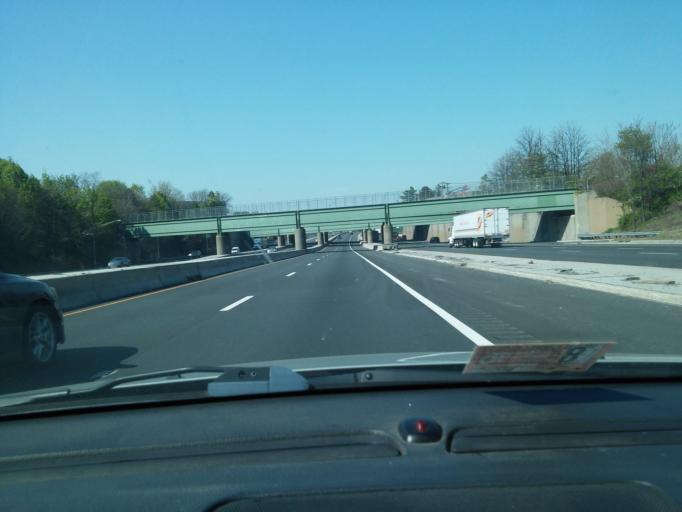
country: US
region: New Jersey
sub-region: Union County
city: Hillside
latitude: 40.7085
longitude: -74.2309
